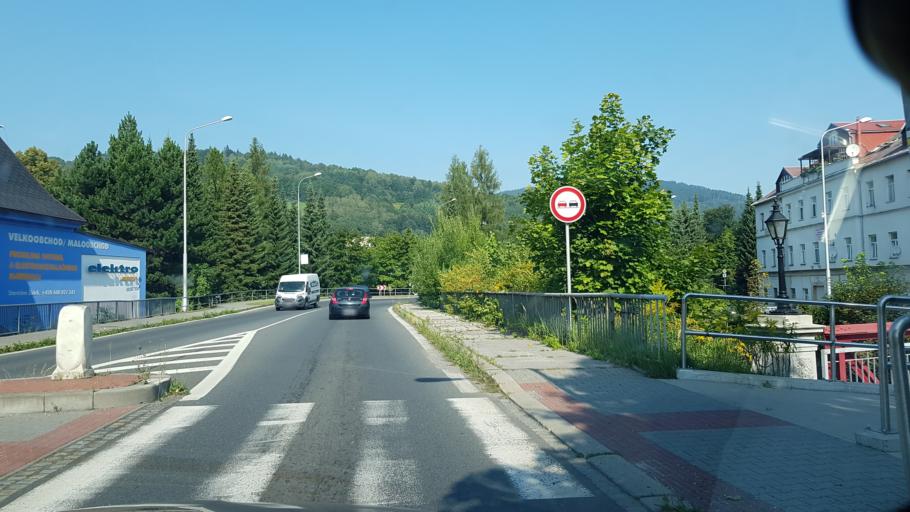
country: CZ
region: Olomoucky
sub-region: Okres Jesenik
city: Jesenik
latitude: 50.2316
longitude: 17.2074
